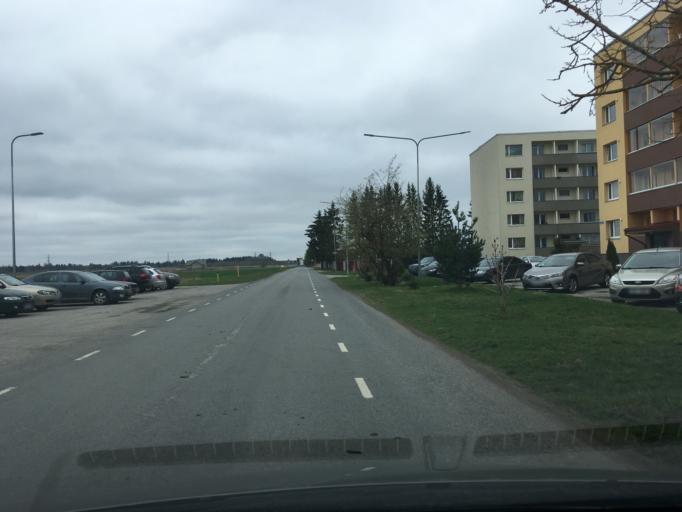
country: EE
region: Harju
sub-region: Rae vald
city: Vaida
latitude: 59.2880
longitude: 24.9803
